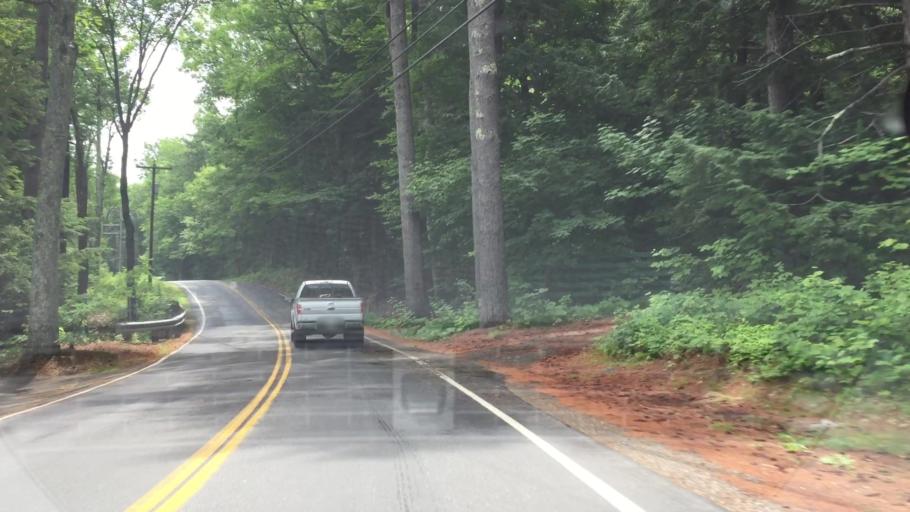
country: US
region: New Hampshire
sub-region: Grafton County
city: Holderness
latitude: 43.7624
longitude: -71.5592
